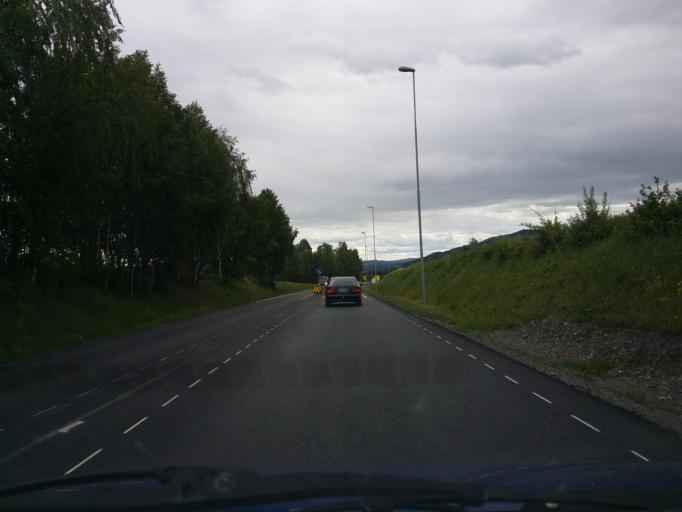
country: NO
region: Hedmark
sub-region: Ringsaker
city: Moelv
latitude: 60.9744
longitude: 10.5896
